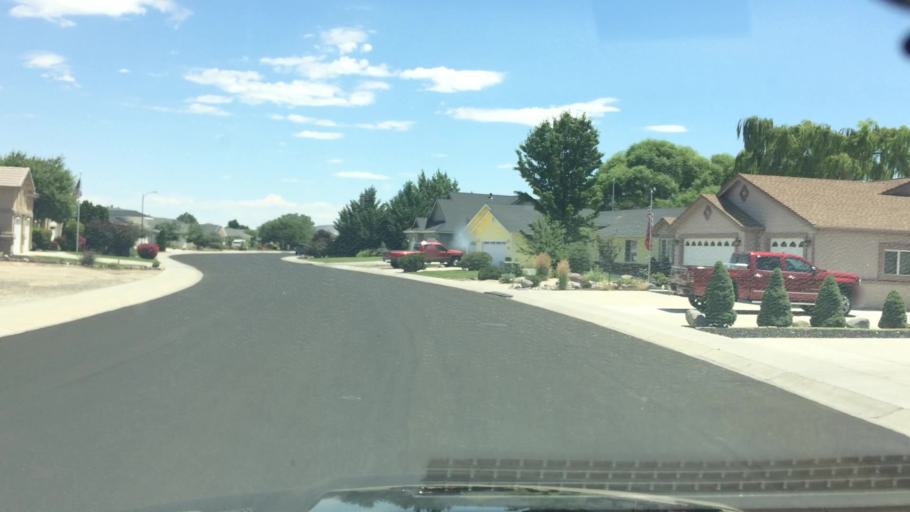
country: US
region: Nevada
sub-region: Lyon County
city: Fernley
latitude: 39.5842
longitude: -119.1471
